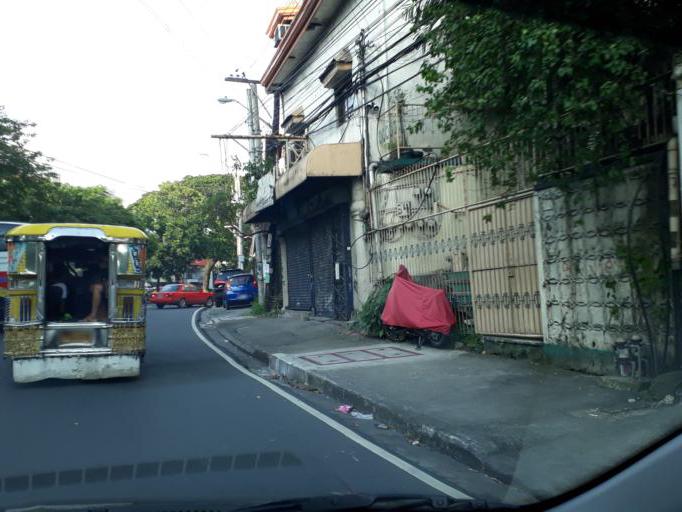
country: PH
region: Calabarzon
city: Bagong Pagasa
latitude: 14.6628
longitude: 121.0207
